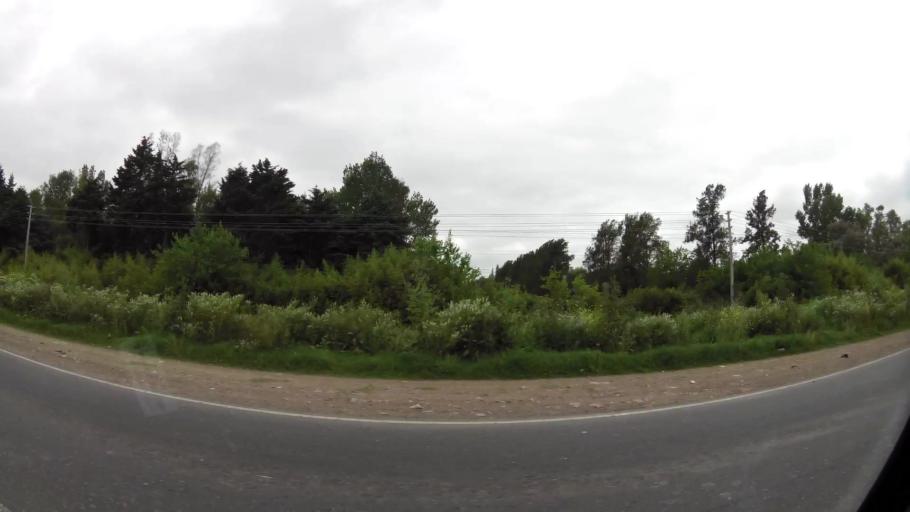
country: AR
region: Buenos Aires
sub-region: Partido de Ezeiza
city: Ezeiza
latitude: -34.8945
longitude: -58.5078
